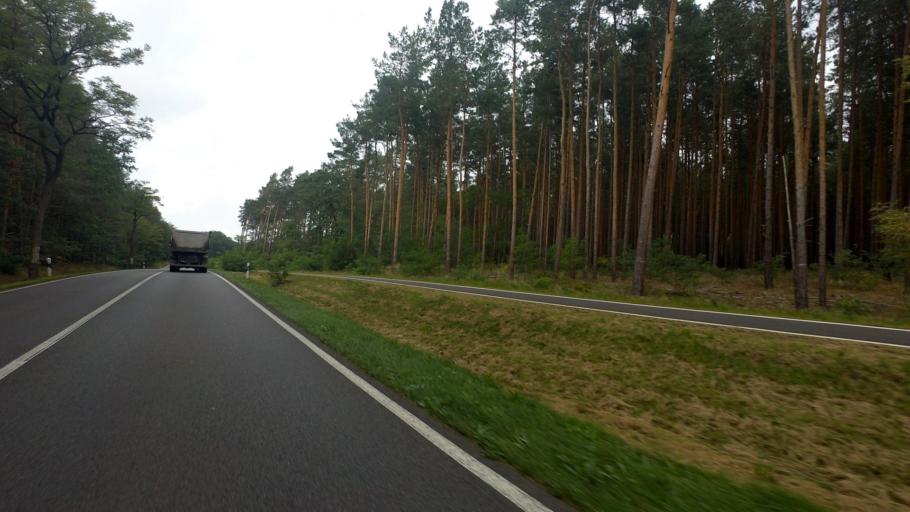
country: DE
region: Brandenburg
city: Schilda
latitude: 51.5577
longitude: 13.3737
